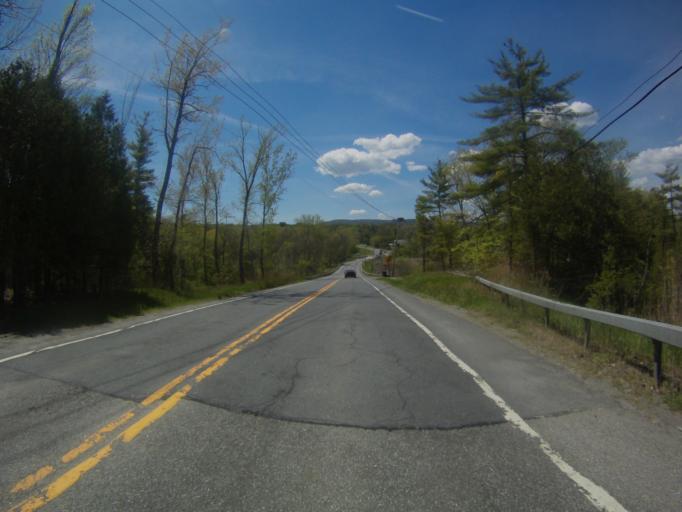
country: US
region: New York
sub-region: Essex County
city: Port Henry
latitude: 43.9585
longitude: -73.4306
